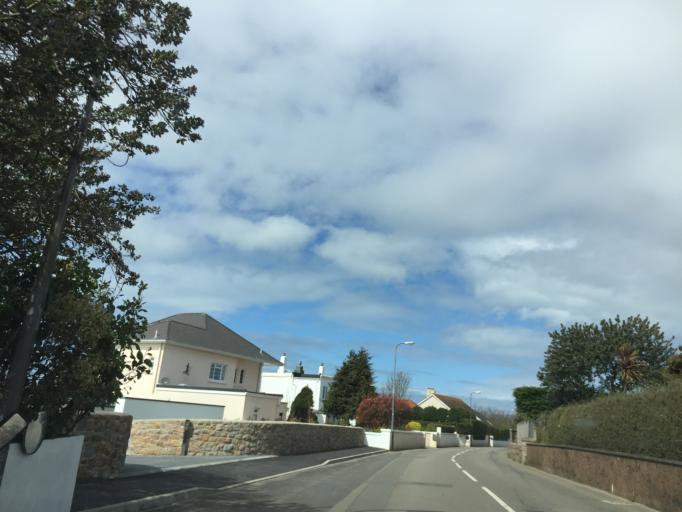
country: JE
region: St Helier
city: Saint Helier
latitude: 49.1803
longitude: -2.1761
